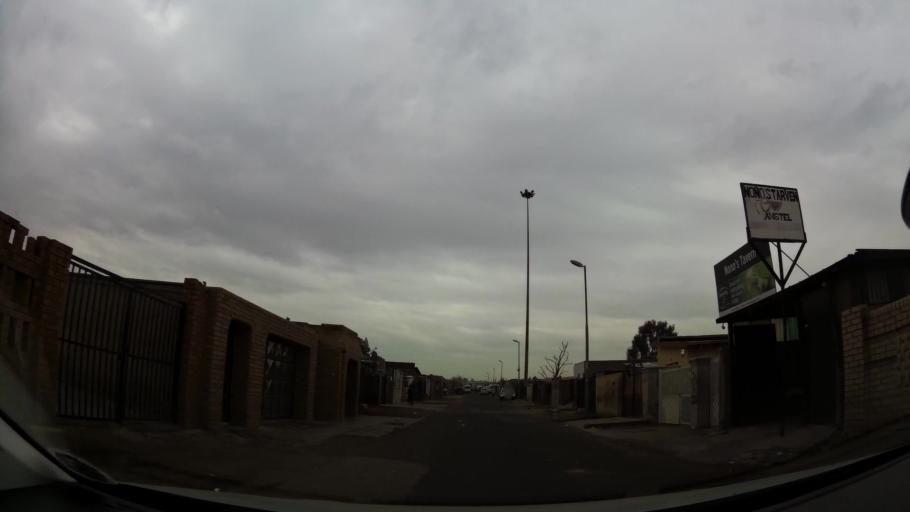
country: ZA
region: Gauteng
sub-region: City of Johannesburg Metropolitan Municipality
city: Soweto
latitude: -26.2557
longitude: 27.8762
